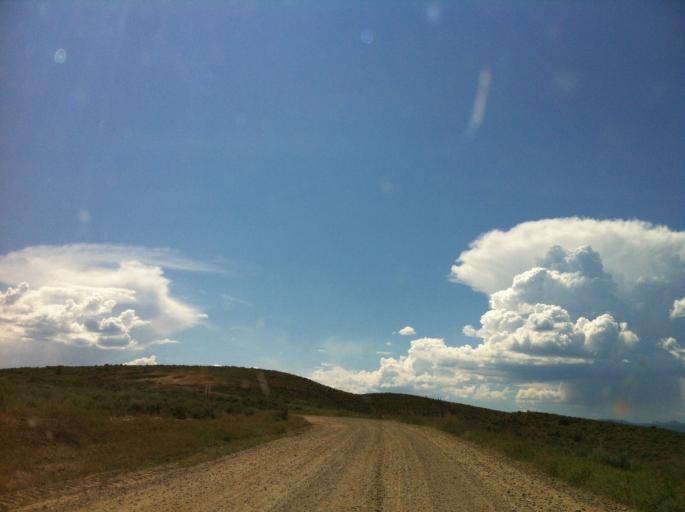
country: US
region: Oregon
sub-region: Baker County
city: Baker City
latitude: 44.7068
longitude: -117.7868
